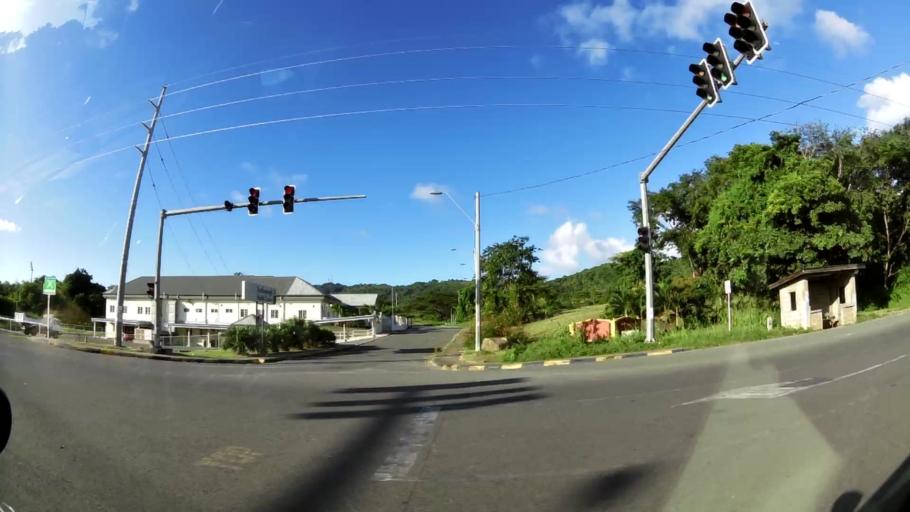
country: TT
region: Tobago
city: Scarborough
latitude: 11.1801
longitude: -60.7131
